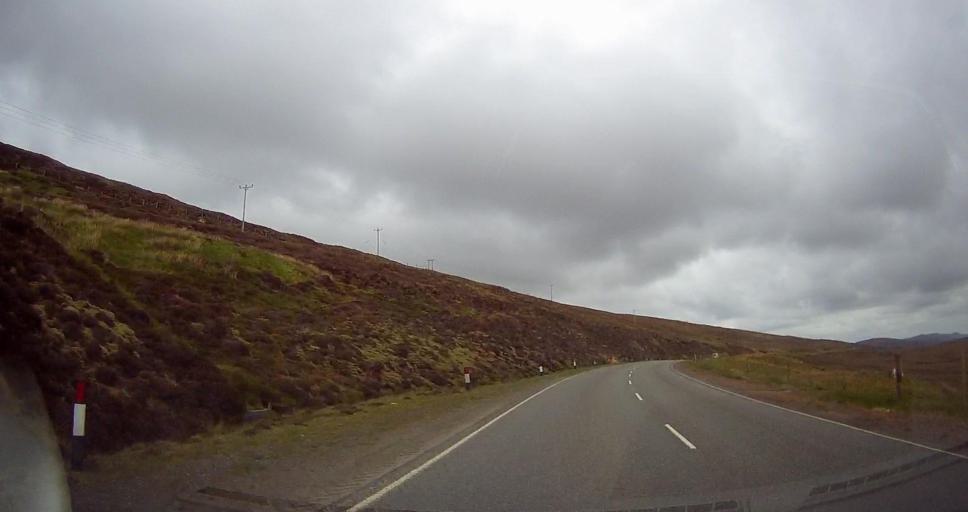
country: GB
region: Scotland
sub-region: Shetland Islands
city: Lerwick
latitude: 60.3057
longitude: -1.2406
